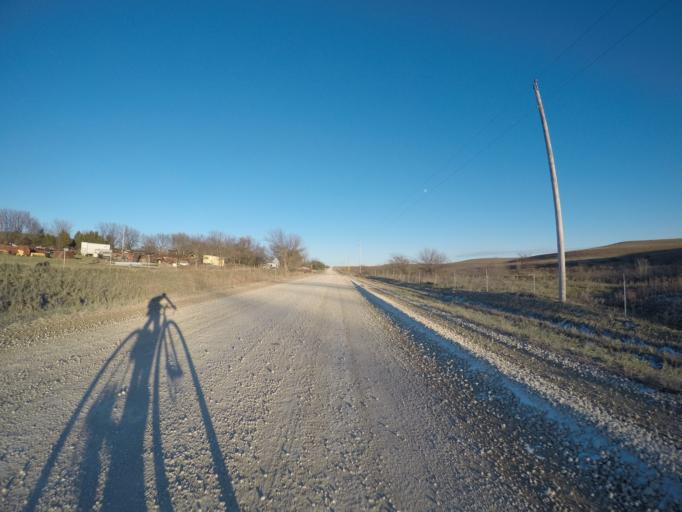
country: US
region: Kansas
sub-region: Riley County
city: Manhattan
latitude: 39.3198
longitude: -96.5370
